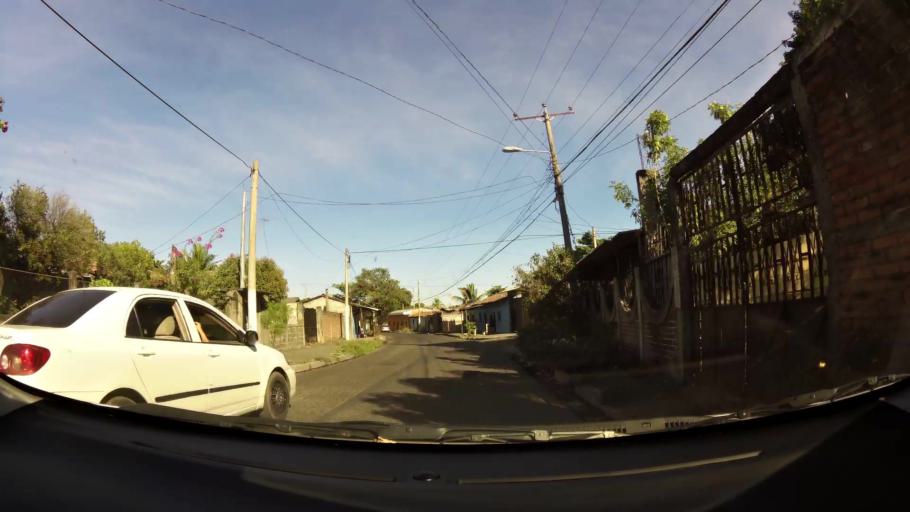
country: SV
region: San Miguel
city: San Miguel
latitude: 13.4691
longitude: -88.1896
